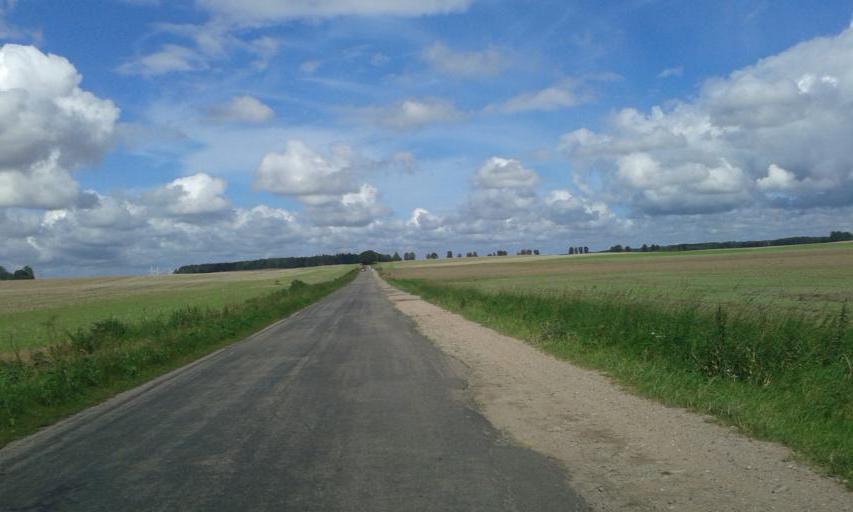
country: PL
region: West Pomeranian Voivodeship
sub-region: Powiat slawienski
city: Slawno
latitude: 54.2849
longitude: 16.6628
